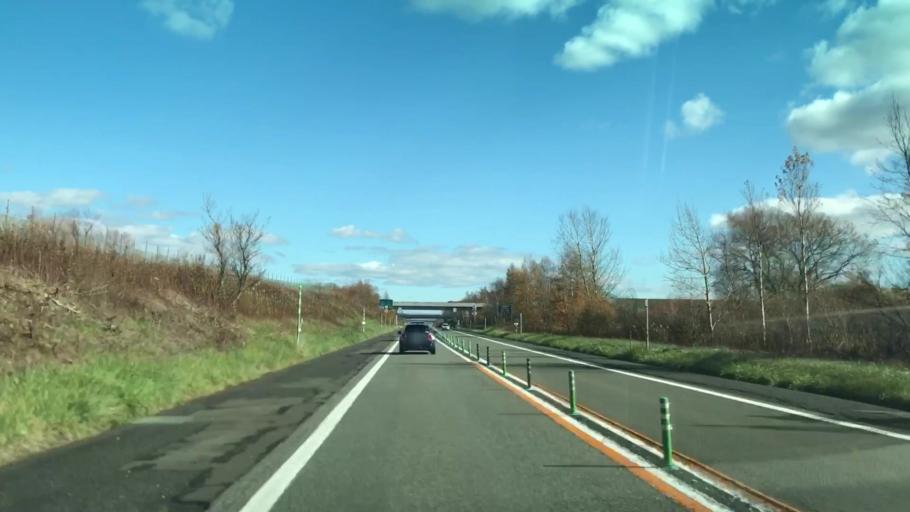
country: JP
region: Hokkaido
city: Chitose
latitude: 42.8931
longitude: 141.7988
